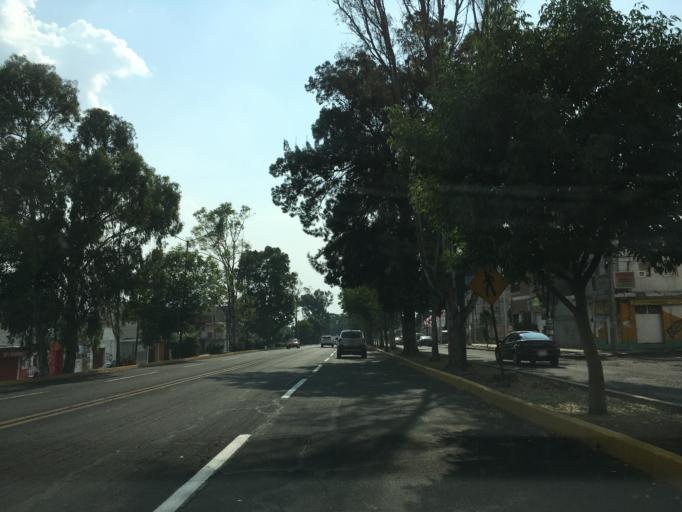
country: MX
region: Michoacan
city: Morelia
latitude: 19.6957
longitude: -101.1603
